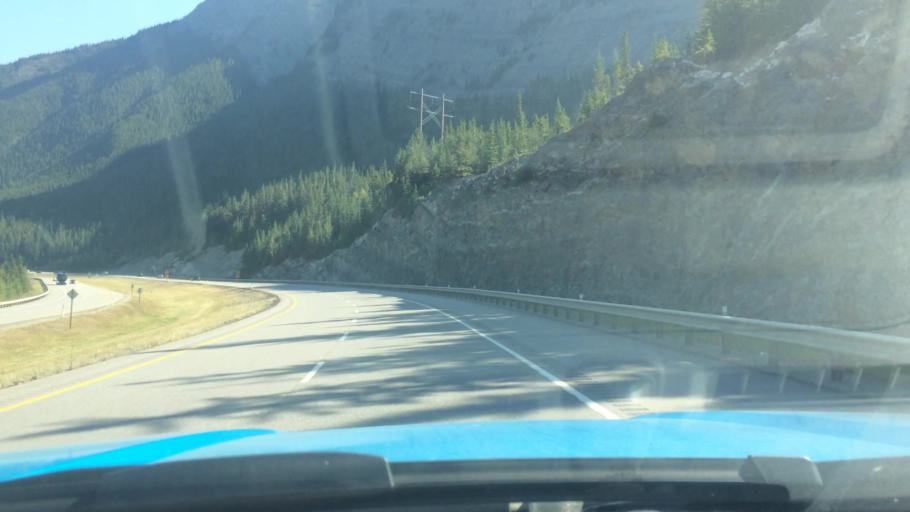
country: CA
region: Alberta
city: Canmore
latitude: 51.0506
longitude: -115.1894
